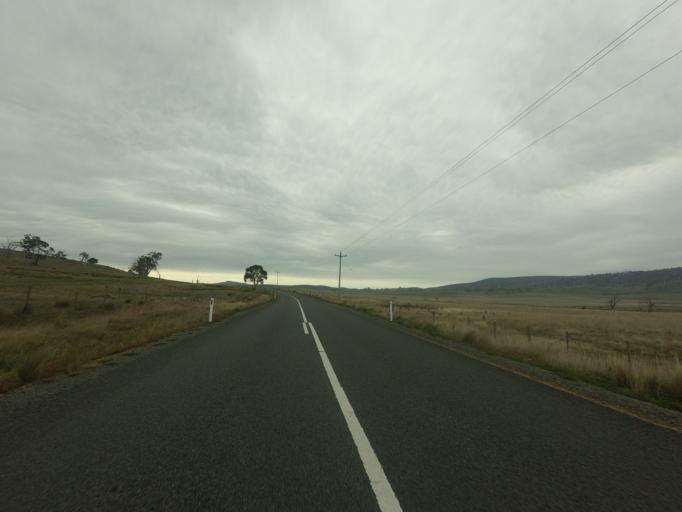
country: AU
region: Tasmania
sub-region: Derwent Valley
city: New Norfolk
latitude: -42.4352
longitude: 146.9835
